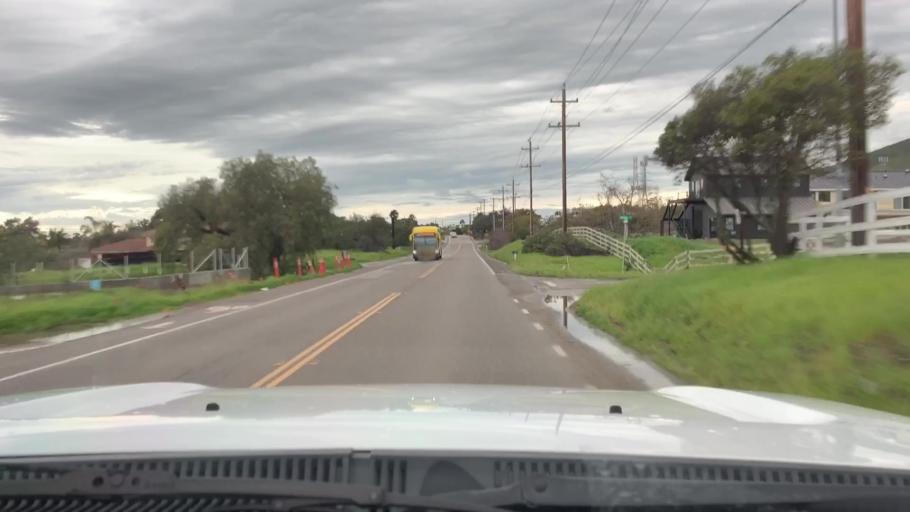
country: US
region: California
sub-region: San Luis Obispo County
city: San Luis Obispo
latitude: 35.2584
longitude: -120.6327
